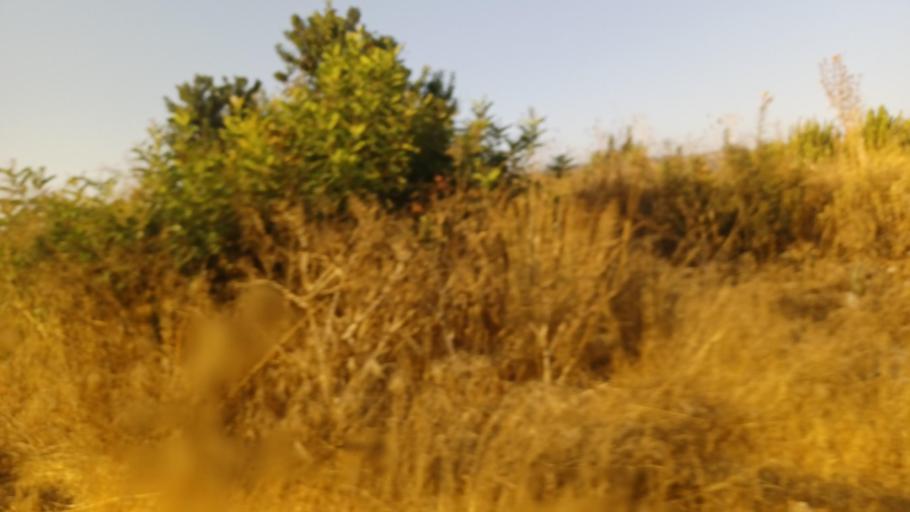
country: CY
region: Pafos
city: Polis
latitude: 34.9743
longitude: 32.4302
